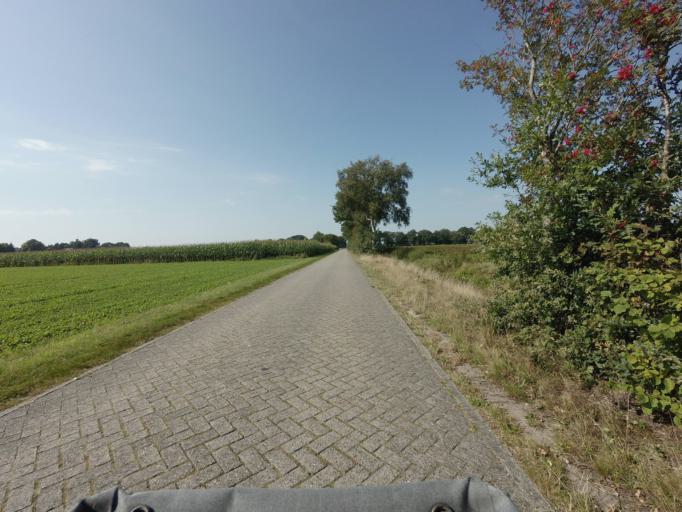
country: DE
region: Lower Saxony
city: Emlichheim
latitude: 52.5788
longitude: 6.8299
